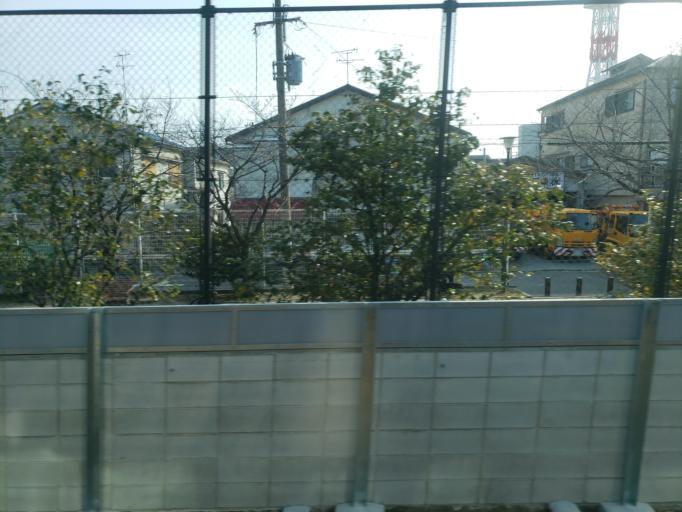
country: JP
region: Hyogo
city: Nishinomiya-hama
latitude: 34.7389
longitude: 135.3663
